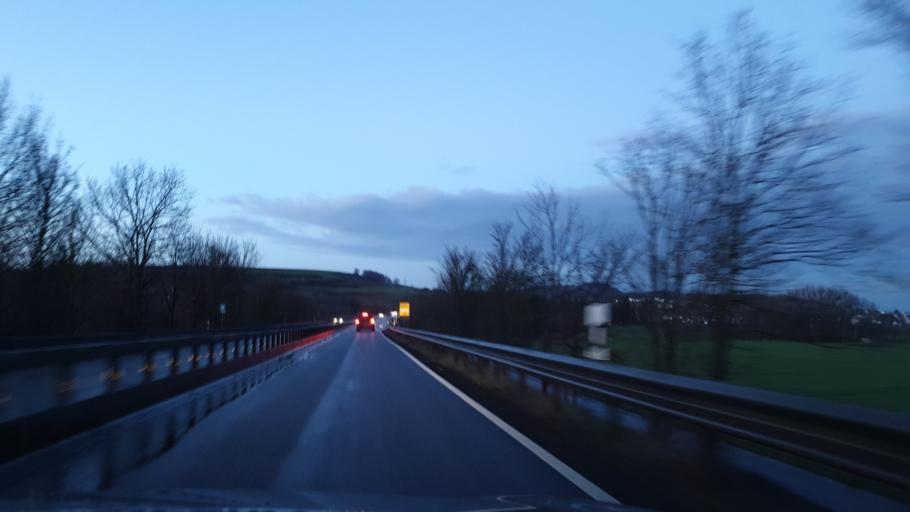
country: DE
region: Rheinland-Pfalz
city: Kottenheim
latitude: 50.3437
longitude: 7.2663
